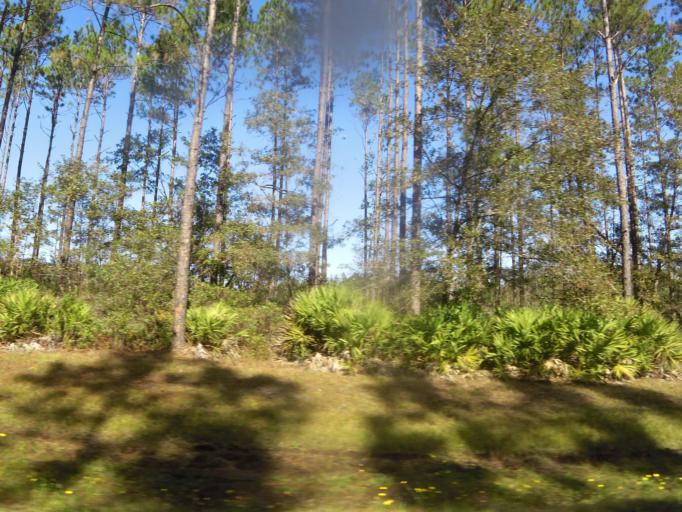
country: US
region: Georgia
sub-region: Charlton County
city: Folkston
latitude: 30.7396
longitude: -82.1064
